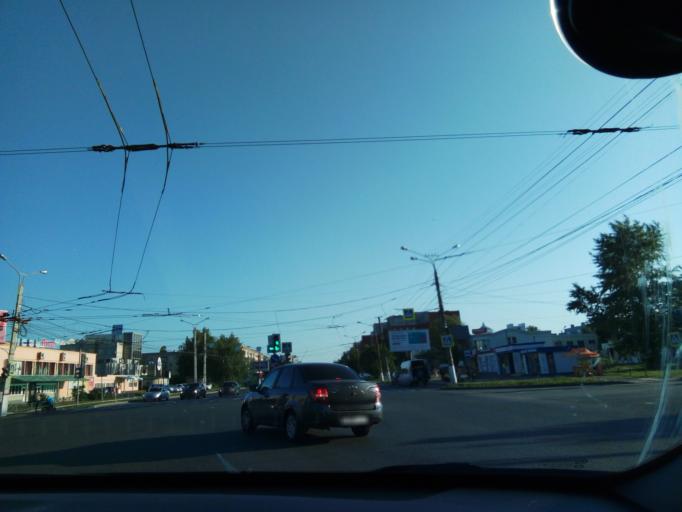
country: RU
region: Chuvashia
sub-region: Cheboksarskiy Rayon
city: Cheboksary
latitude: 56.1128
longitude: 47.2704
